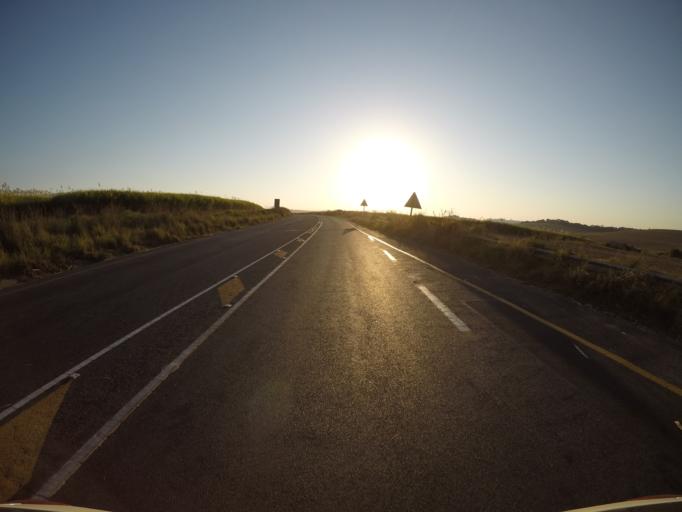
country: ZA
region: KwaZulu-Natal
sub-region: uThungulu District Municipality
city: eSikhawini
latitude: -28.9467
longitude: 31.7345
